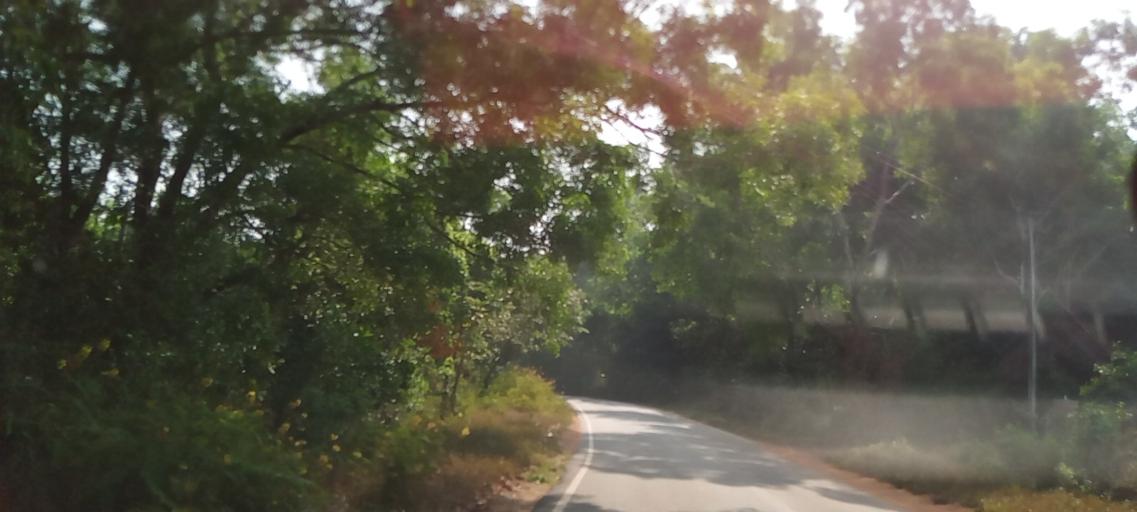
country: IN
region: Karnataka
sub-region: Udupi
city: Manipala
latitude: 13.5132
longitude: 74.8073
